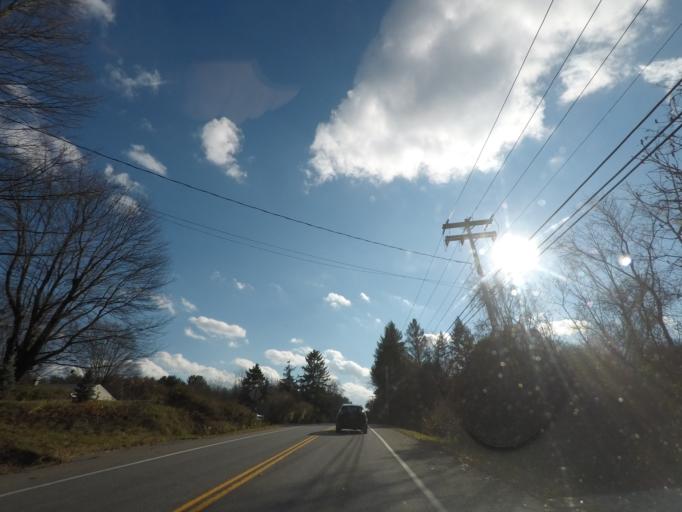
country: US
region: New York
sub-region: Schenectady County
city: East Glenville
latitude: 42.8799
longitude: -73.8874
